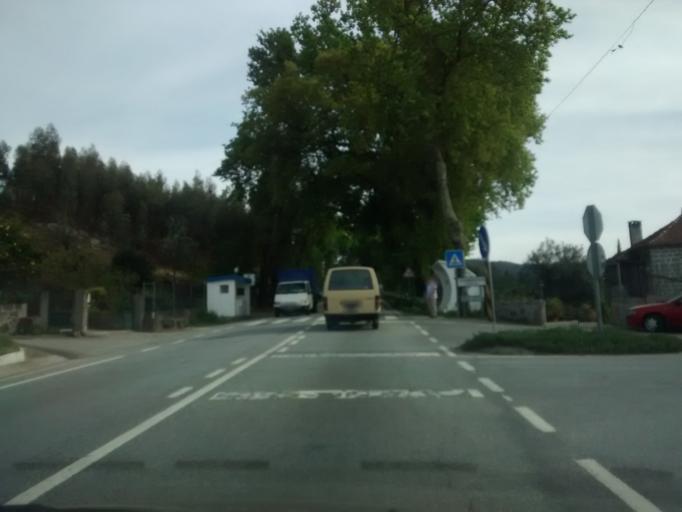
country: PT
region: Braga
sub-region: Braga
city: Braga
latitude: 41.5019
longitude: -8.4164
